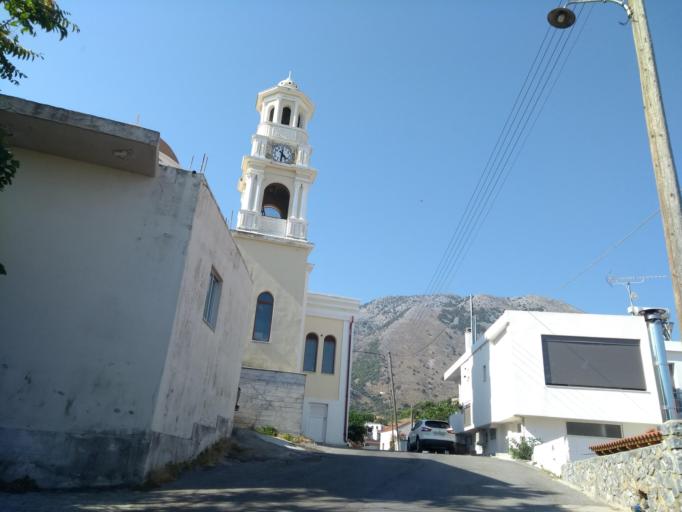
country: GR
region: Crete
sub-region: Nomos Chanias
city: Georgioupolis
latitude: 35.3154
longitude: 24.2956
